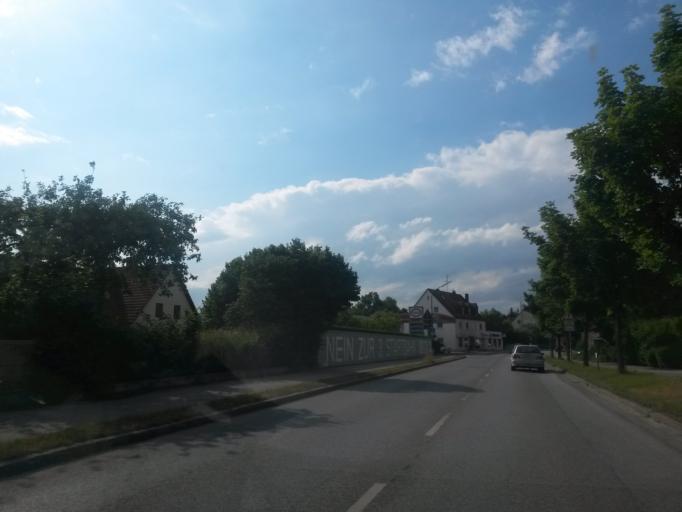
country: DE
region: Bavaria
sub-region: Upper Bavaria
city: Fahrenzhausen
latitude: 48.3483
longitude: 11.5652
